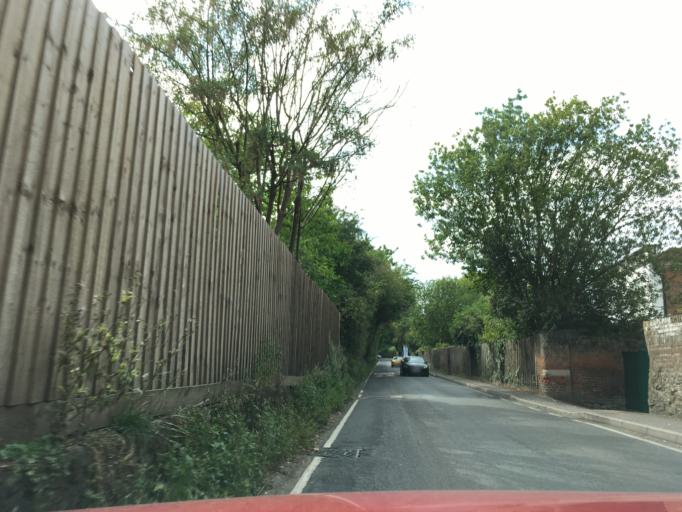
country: GB
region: England
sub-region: Kent
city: Maidstone
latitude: 51.2525
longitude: 0.4788
